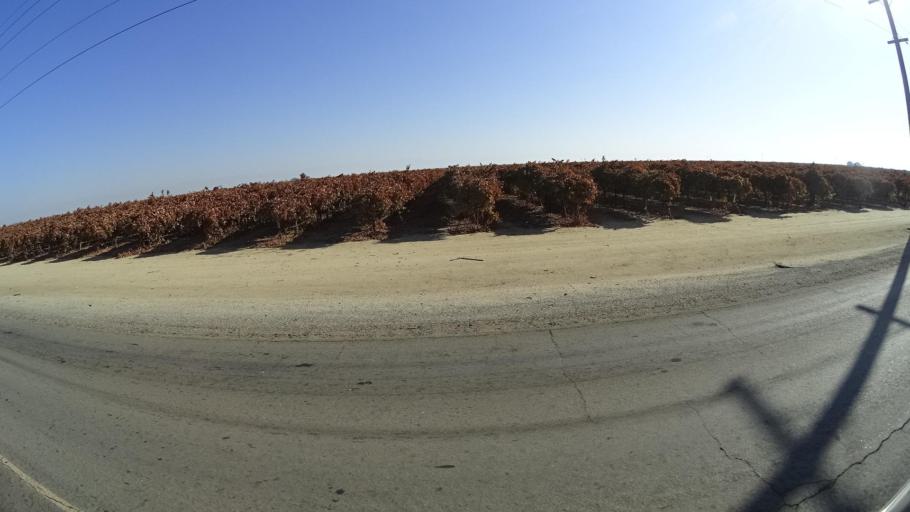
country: US
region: California
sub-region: Kern County
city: Delano
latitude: 35.7353
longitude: -119.2052
